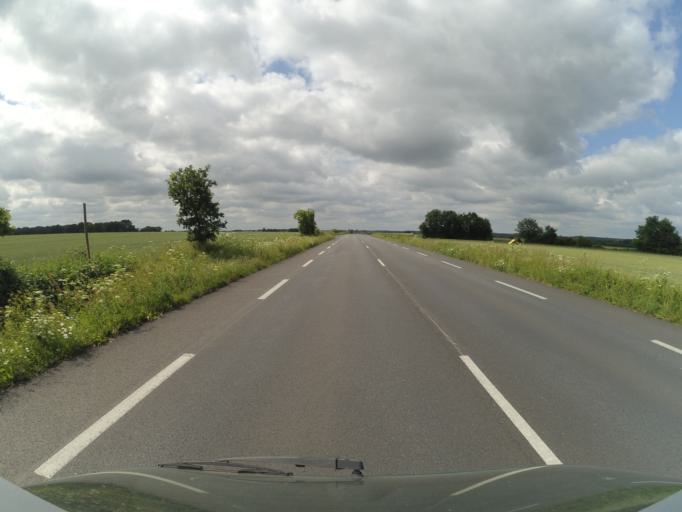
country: FR
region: Pays de la Loire
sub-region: Departement de la Vendee
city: Vendrennes
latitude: 46.8155
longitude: -1.1442
